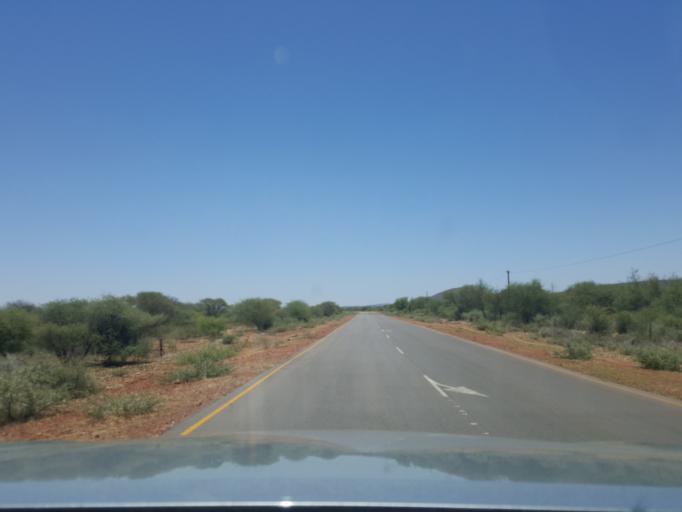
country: BW
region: South East
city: Ramotswa
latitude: -25.0027
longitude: 25.8998
